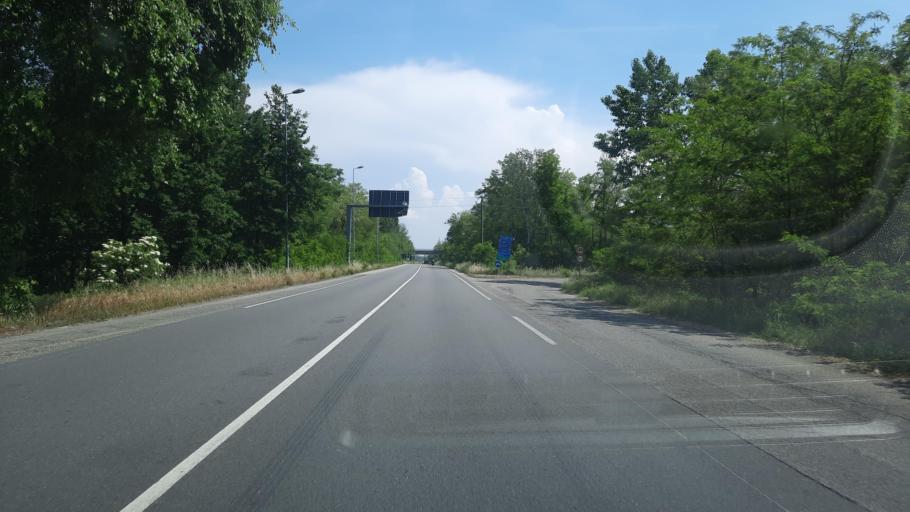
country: IT
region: Lombardy
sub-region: Provincia di Pavia
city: Gropello Cairoli
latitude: 45.1780
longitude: 8.9688
